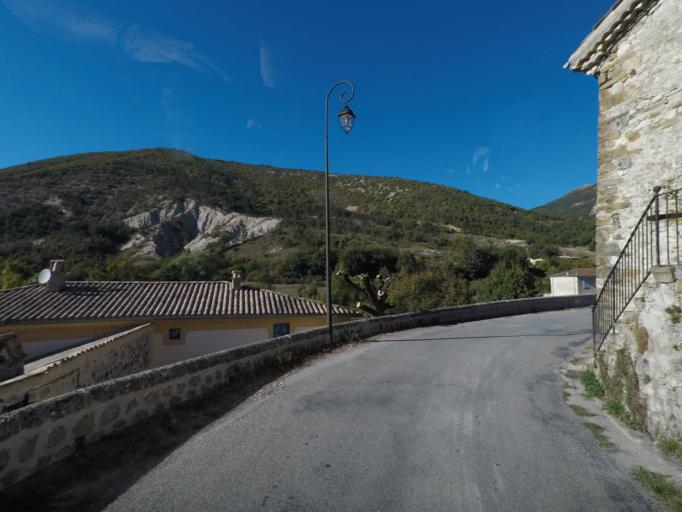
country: FR
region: Rhone-Alpes
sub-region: Departement de la Drome
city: Buis-les-Baronnies
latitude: 44.4701
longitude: 5.4498
